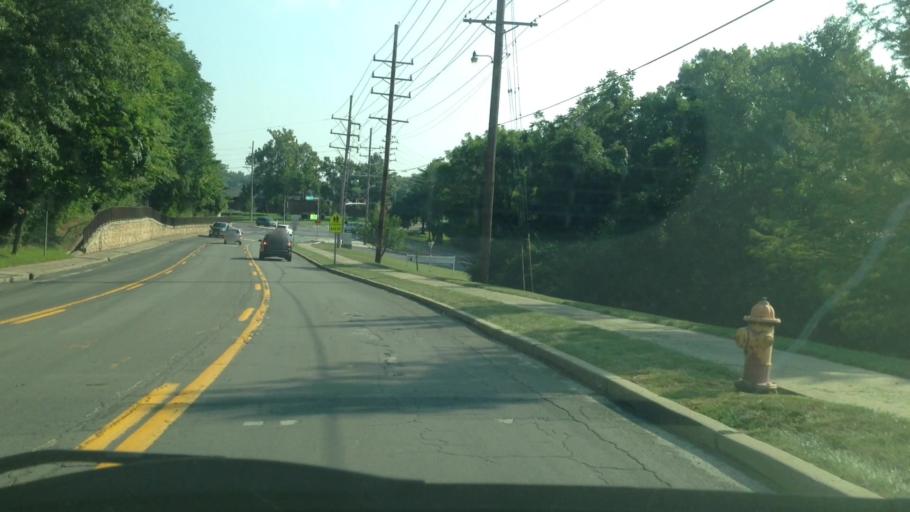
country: US
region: Missouri
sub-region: Saint Louis County
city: Des Peres
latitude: 38.5831
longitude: -90.4447
